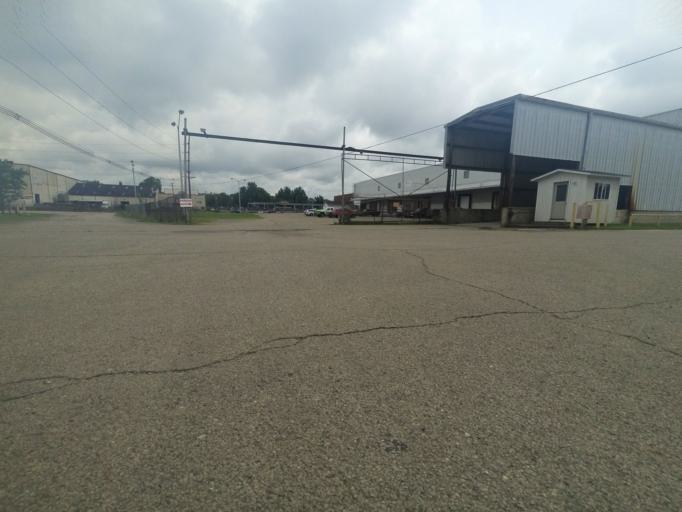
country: US
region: West Virginia
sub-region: Cabell County
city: Huntington
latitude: 38.4073
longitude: -82.4661
